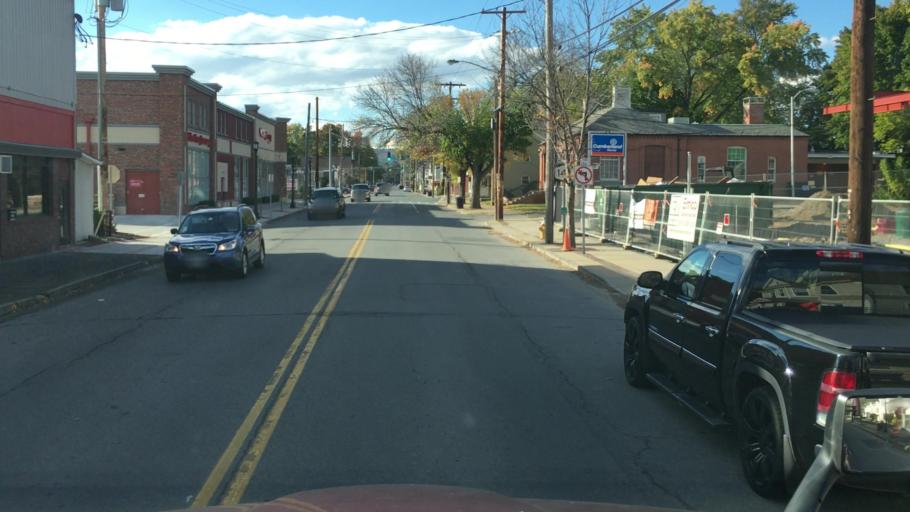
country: US
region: New York
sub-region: Schenectady County
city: Scotia
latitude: 42.8269
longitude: -73.9655
